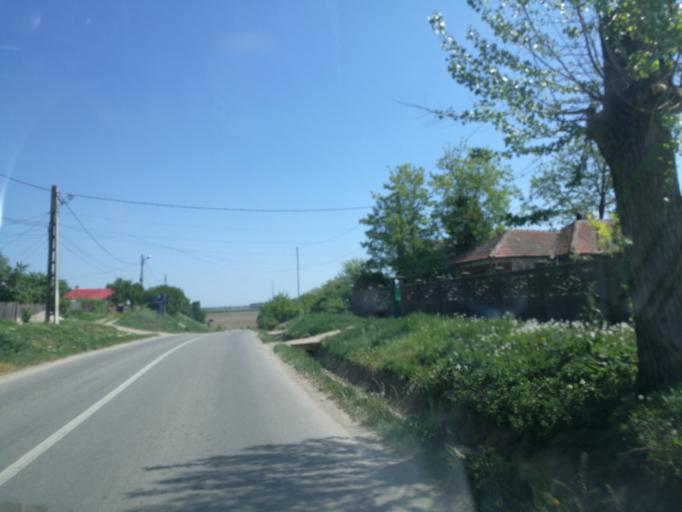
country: RO
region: Ialomita
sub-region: Comuna Maia
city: Maia
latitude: 44.7437
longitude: 26.4080
